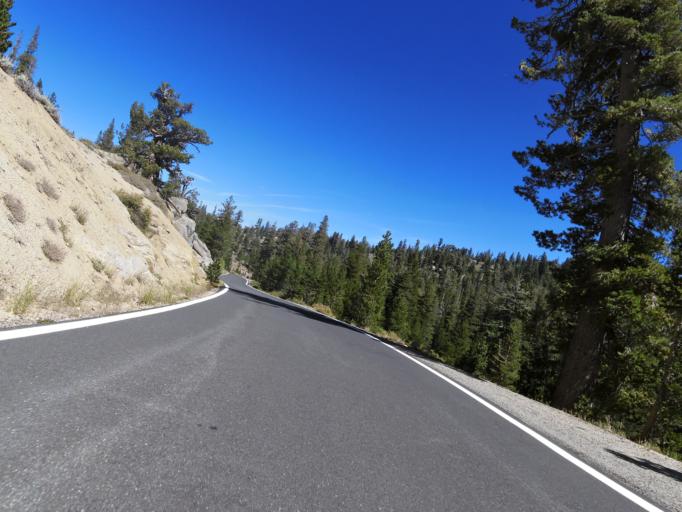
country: US
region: Nevada
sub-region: Douglas County
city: Gardnerville Ranchos
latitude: 38.5630
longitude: -119.8054
